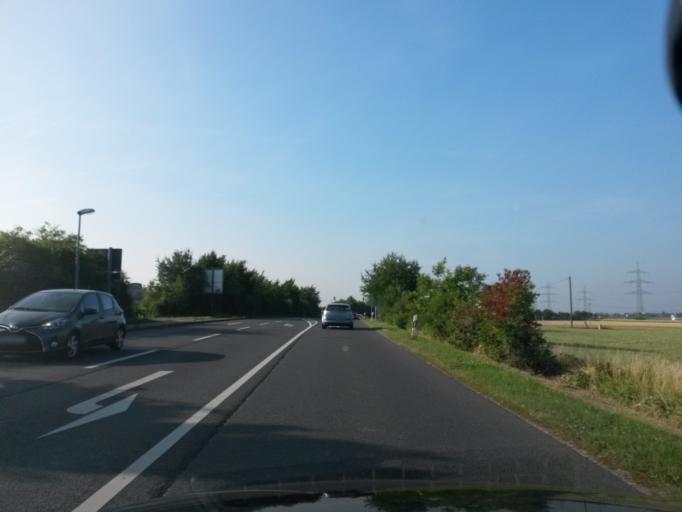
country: DE
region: North Rhine-Westphalia
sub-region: Regierungsbezirk Koln
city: Alfter
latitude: 50.7188
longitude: 7.0299
